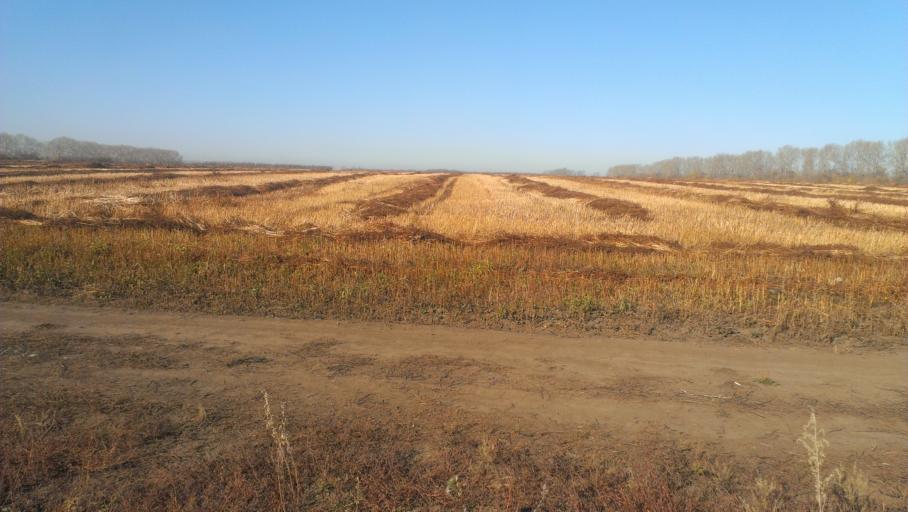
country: RU
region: Altai Krai
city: Novosilikatnyy
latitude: 53.3652
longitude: 83.6405
